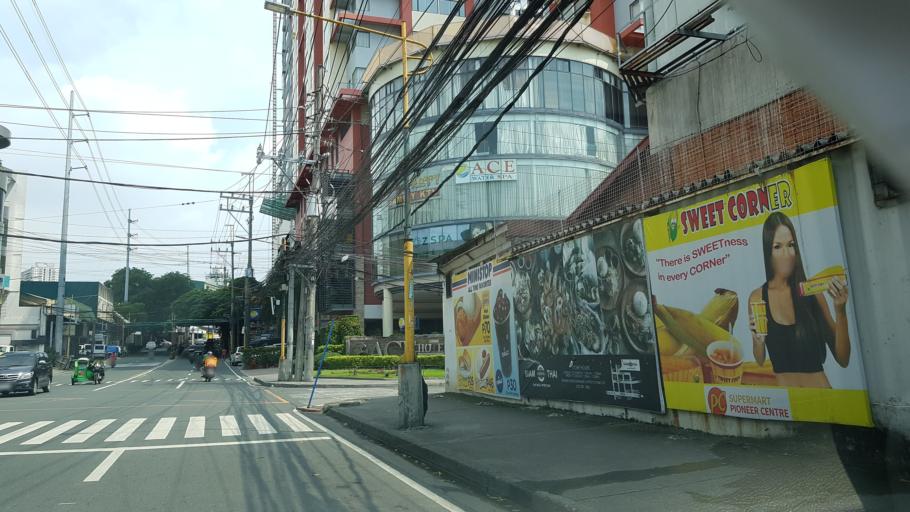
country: PH
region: Metro Manila
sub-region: Pasig
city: Pasig City
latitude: 14.5739
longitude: 121.0588
